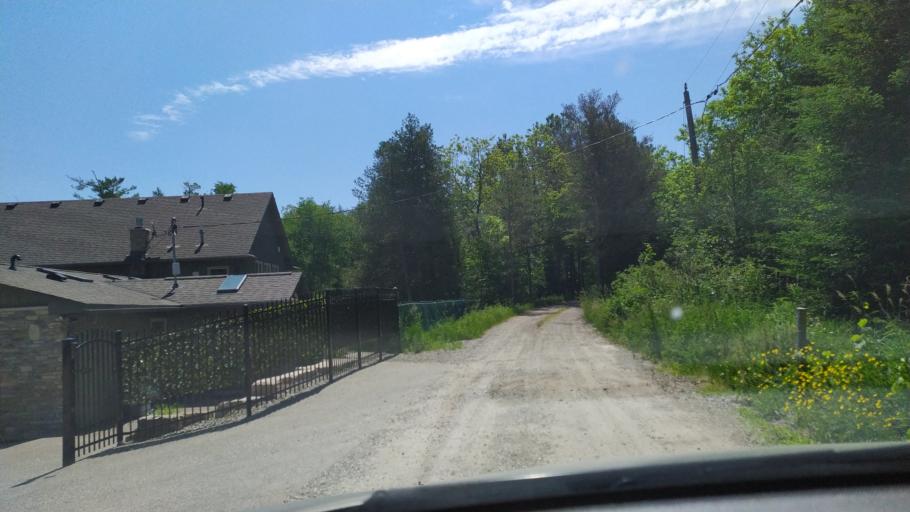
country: CA
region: Ontario
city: Waterloo
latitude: 43.4722
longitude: -80.6343
